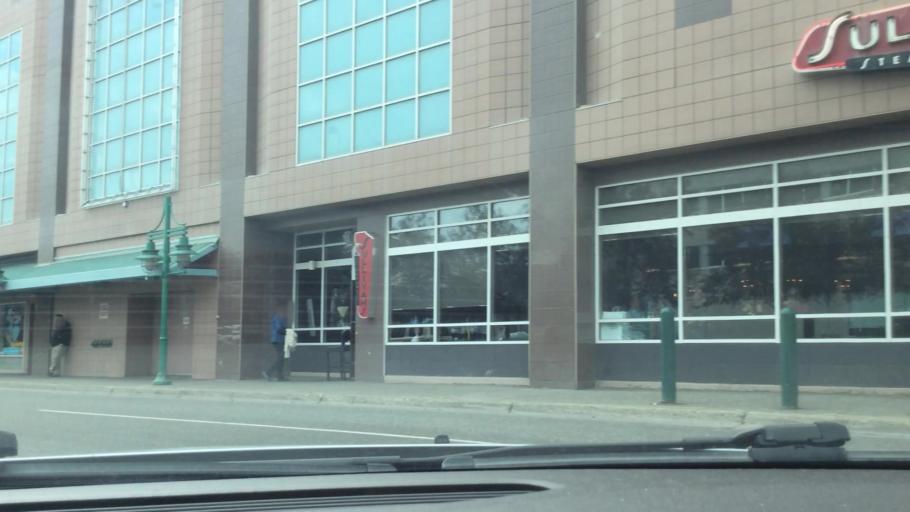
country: US
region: Alaska
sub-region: Anchorage Municipality
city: Anchorage
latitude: 61.2175
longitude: -149.8873
